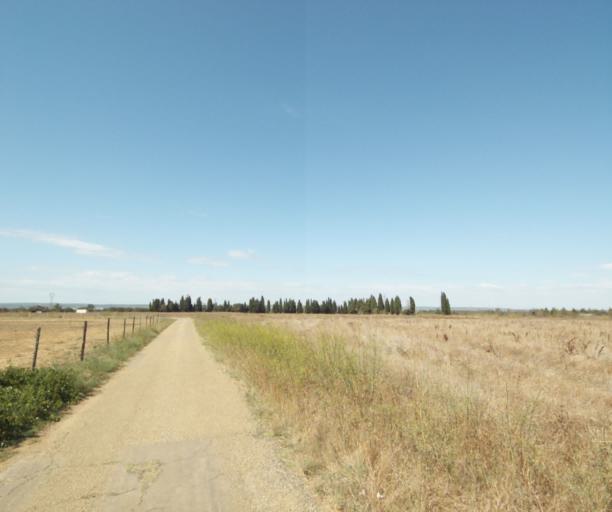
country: FR
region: Languedoc-Roussillon
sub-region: Departement du Gard
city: Bouillargues
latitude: 43.8039
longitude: 4.4508
